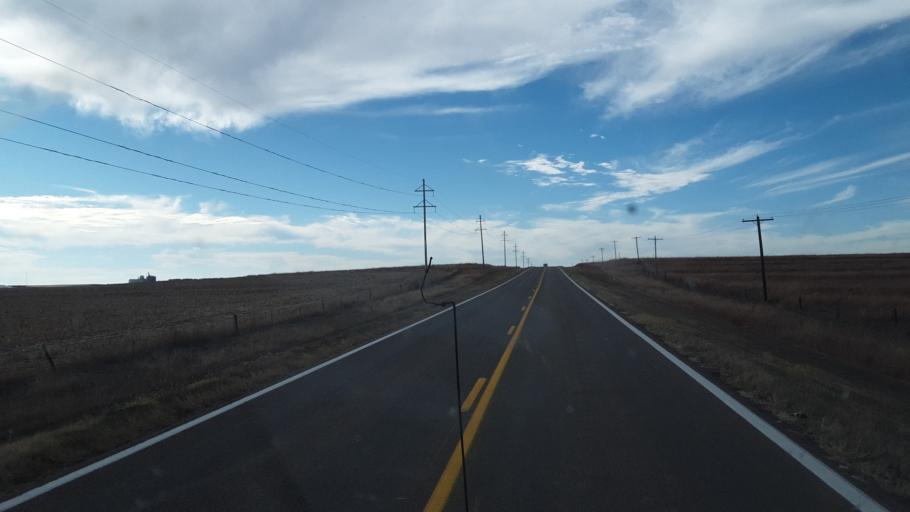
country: US
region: Kansas
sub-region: Hodgeman County
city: Jetmore
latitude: 38.0880
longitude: -99.8674
